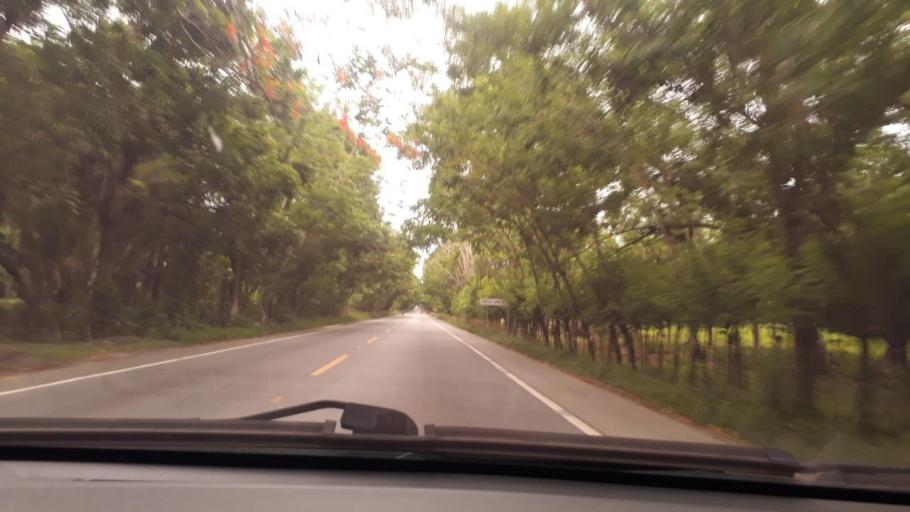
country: GT
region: Izabal
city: Morales
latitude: 15.4766
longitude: -88.8898
